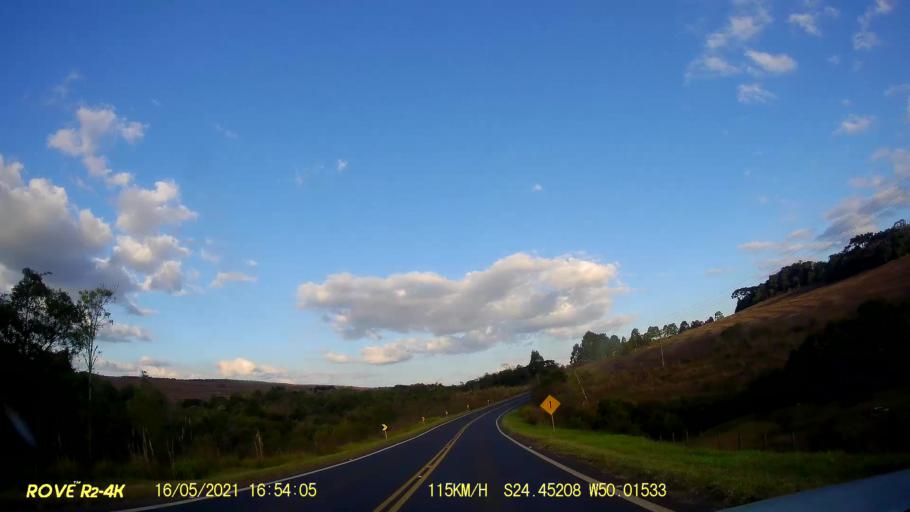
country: BR
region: Parana
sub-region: Pirai Do Sul
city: Pirai do Sul
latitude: -24.4525
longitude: -50.0152
